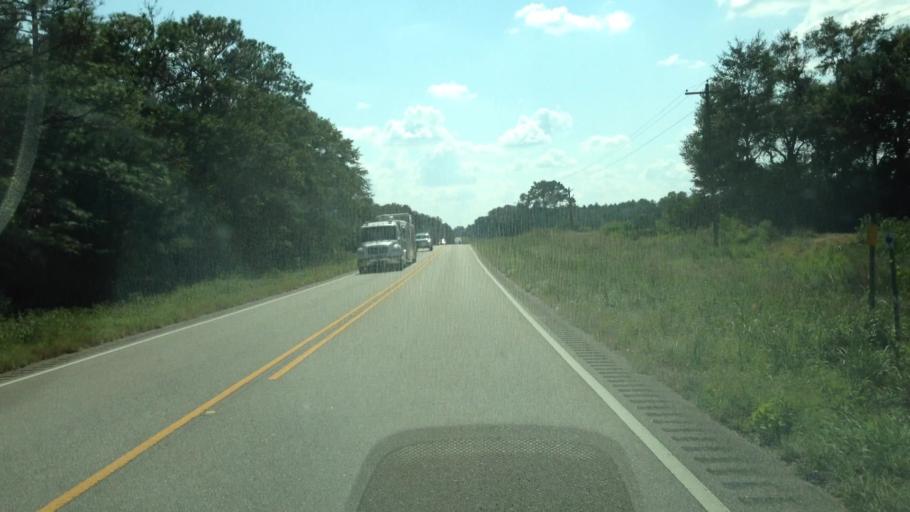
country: US
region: Alabama
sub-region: Covington County
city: Florala
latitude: 31.0406
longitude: -86.5973
